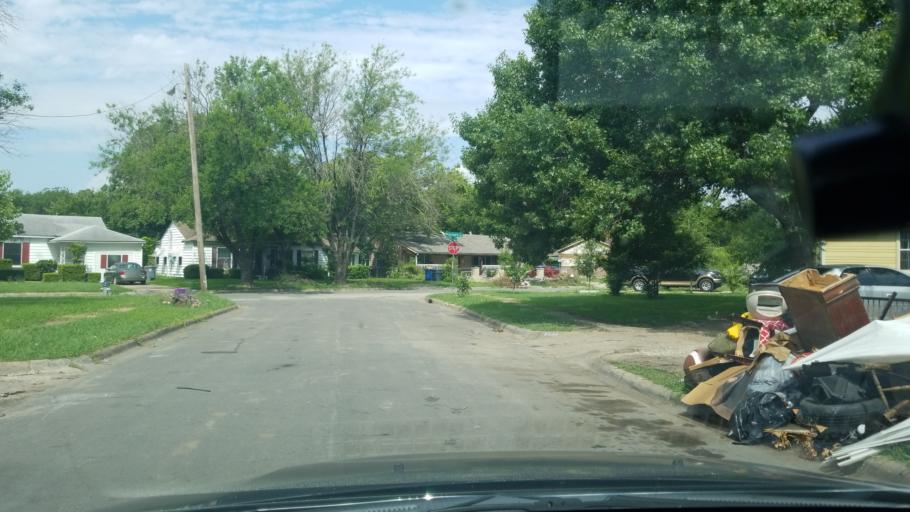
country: US
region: Texas
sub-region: Dallas County
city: Balch Springs
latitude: 32.7366
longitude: -96.6855
